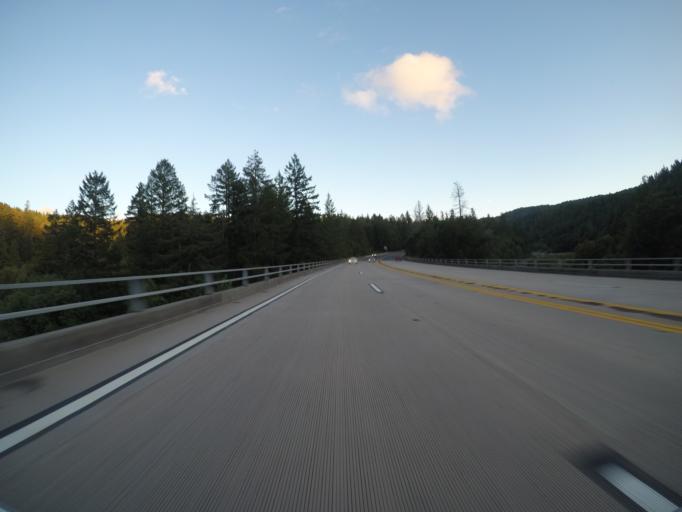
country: US
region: California
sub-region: Humboldt County
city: Redway
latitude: 39.9561
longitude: -123.7801
